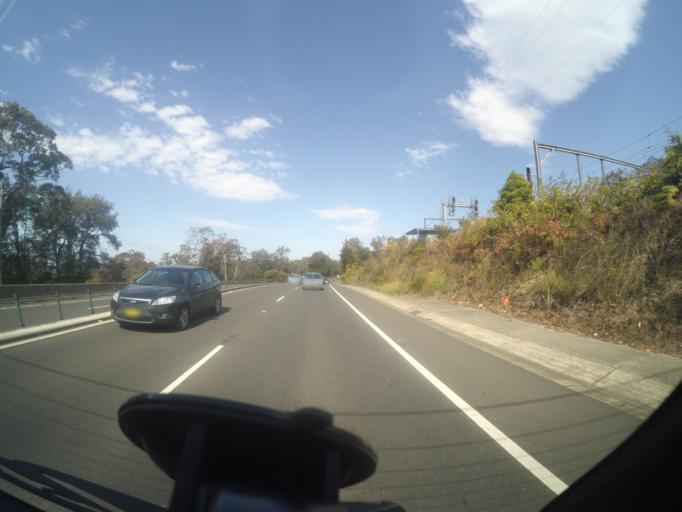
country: AU
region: New South Wales
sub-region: Blue Mountains Municipality
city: Blaxland
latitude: -33.7063
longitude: 150.5853
